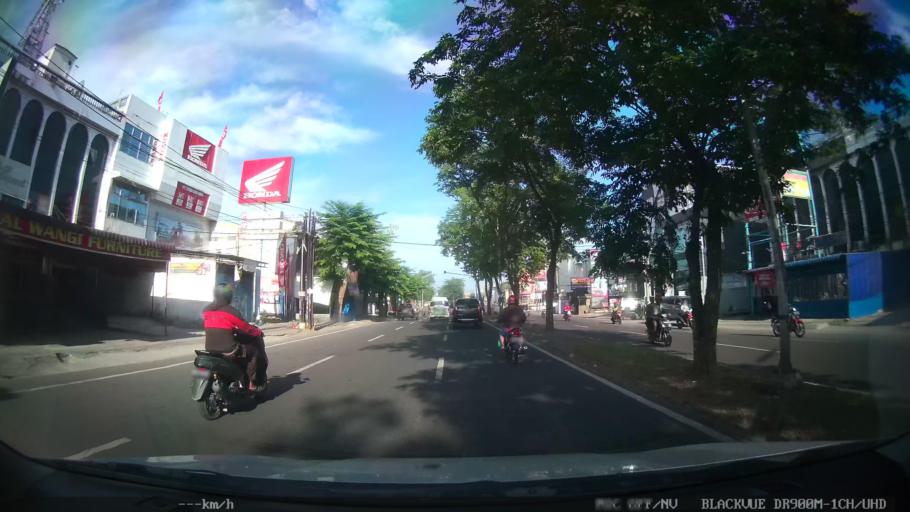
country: ID
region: North Sumatra
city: Medan
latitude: 3.5904
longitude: 98.6481
